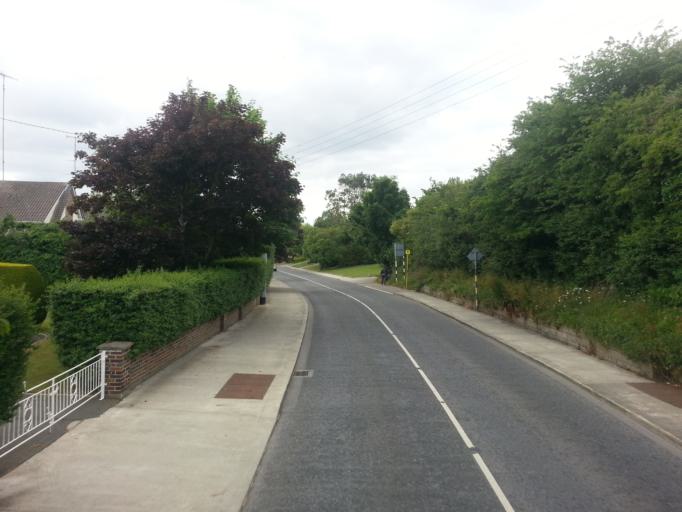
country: IE
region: Leinster
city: Sandyford
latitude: 53.2537
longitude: -6.2144
